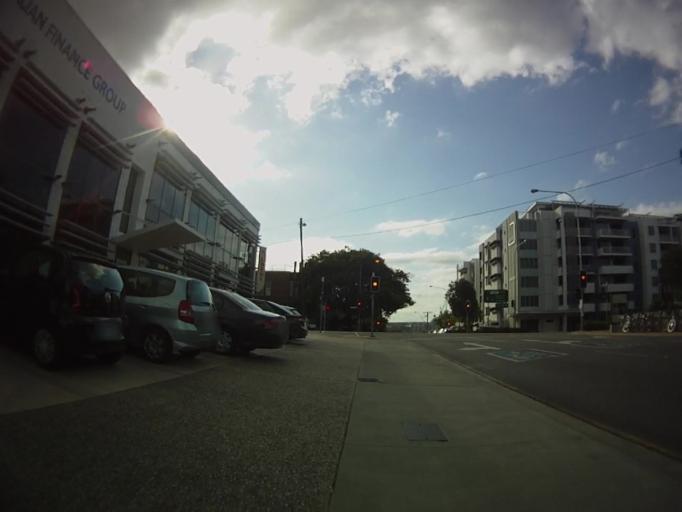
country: AU
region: Queensland
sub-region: Brisbane
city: South Brisbane
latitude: -27.4743
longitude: 153.0145
